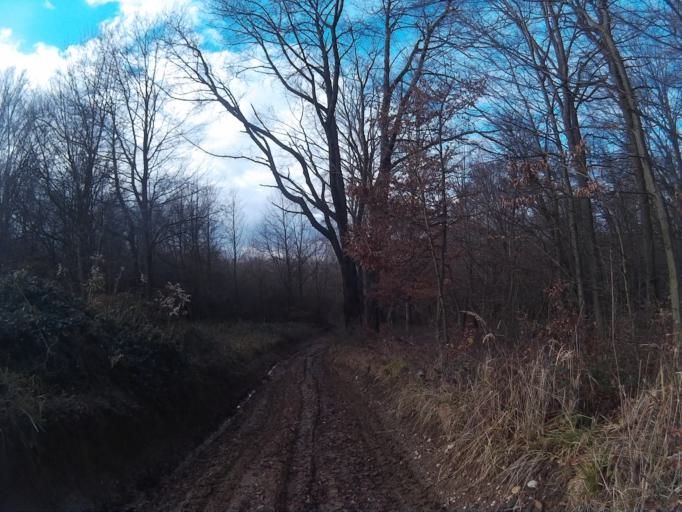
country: HU
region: Veszprem
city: Urkut
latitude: 47.1221
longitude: 17.6703
